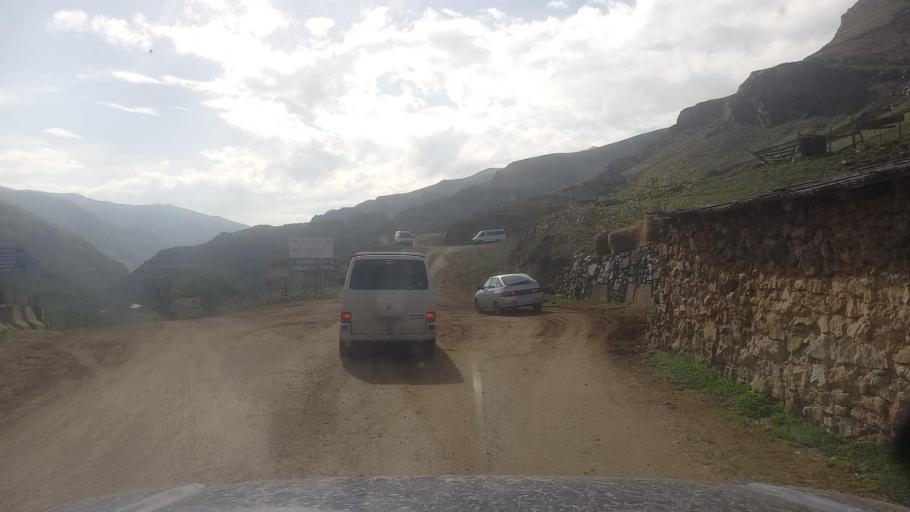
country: RU
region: Kabardino-Balkariya
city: Kamennomostskoye
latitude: 43.7255
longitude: 42.9120
